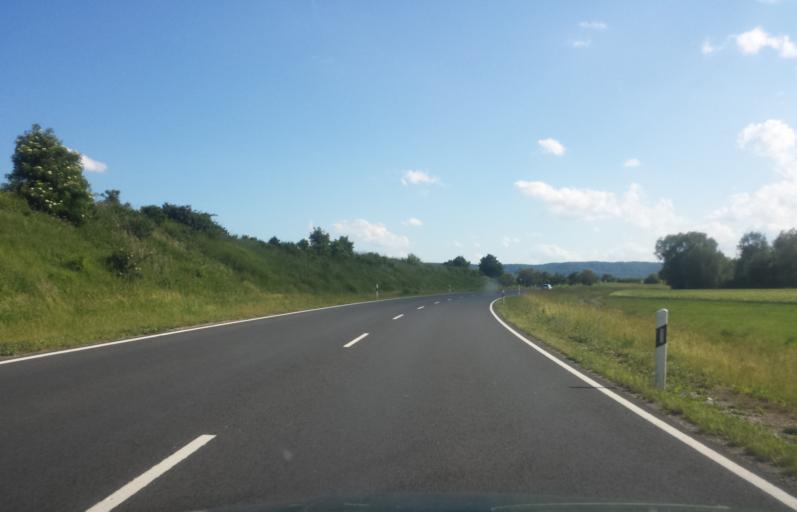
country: DE
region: Bavaria
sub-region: Regierungsbezirk Mittelfranken
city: Illesheim
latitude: 49.4775
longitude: 10.3730
